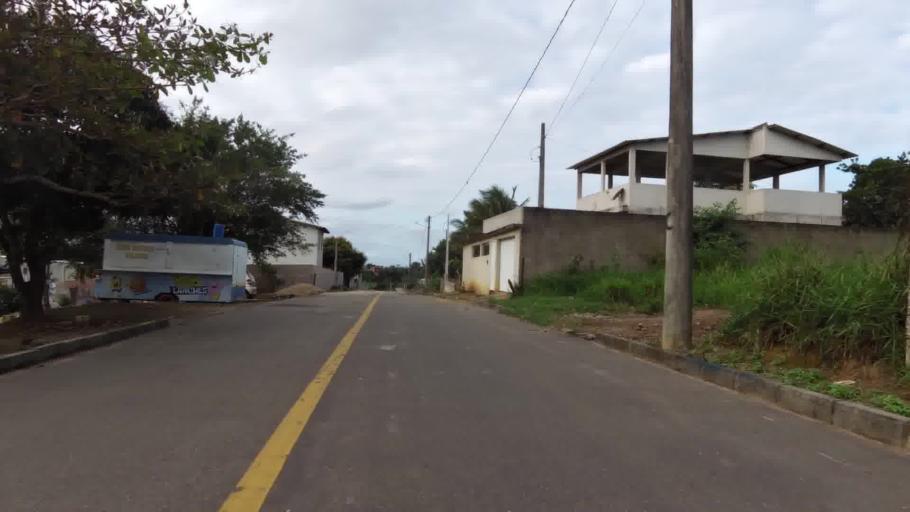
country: BR
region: Espirito Santo
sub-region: Piuma
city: Piuma
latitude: -20.7992
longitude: -40.6450
